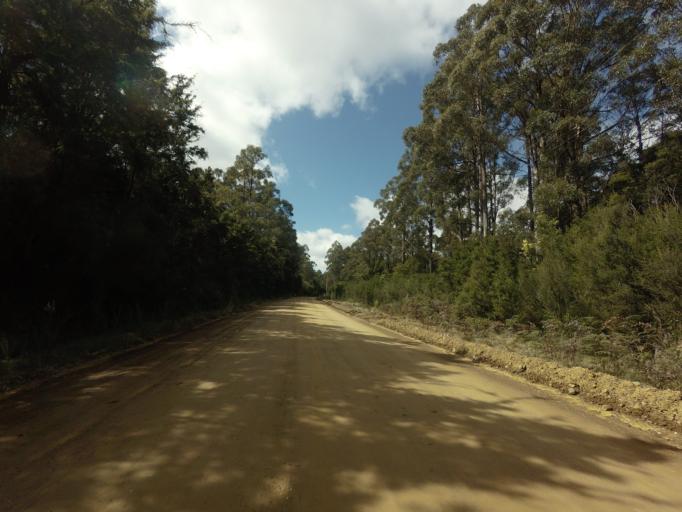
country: AU
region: Tasmania
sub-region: Huon Valley
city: Geeveston
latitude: -43.4135
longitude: 146.8956
